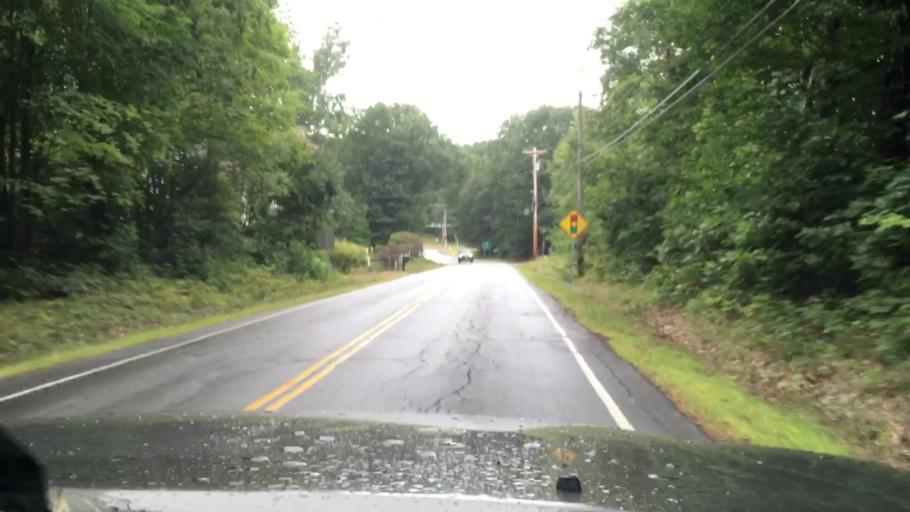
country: US
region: New Hampshire
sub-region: Belknap County
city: Meredith
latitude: 43.6405
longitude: -71.5317
